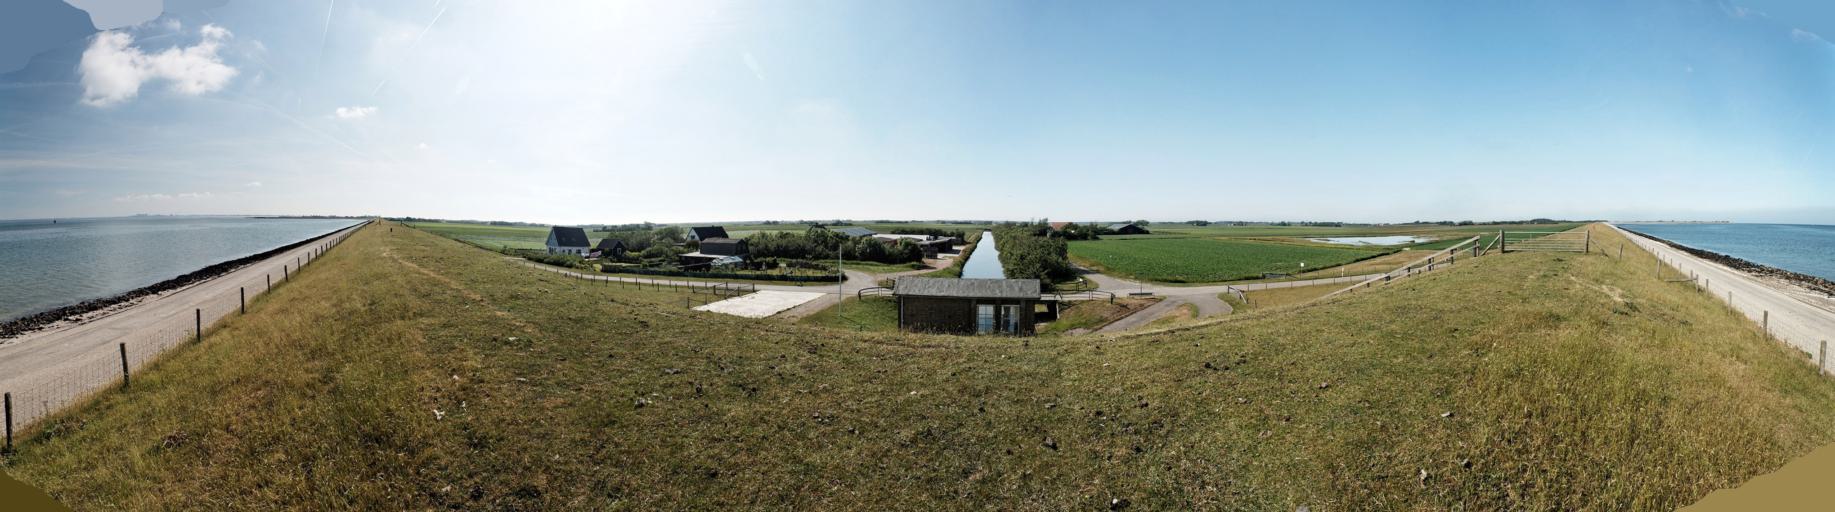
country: NL
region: North Holland
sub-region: Gemeente Texel
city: Den Burg
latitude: 53.0177
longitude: 4.8040
